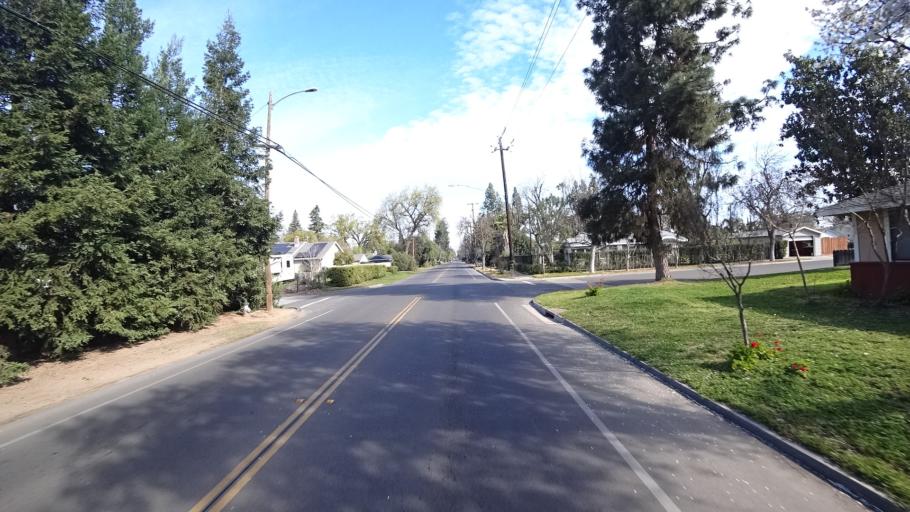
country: US
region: California
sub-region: Fresno County
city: Fresno
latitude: 36.7893
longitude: -119.7996
